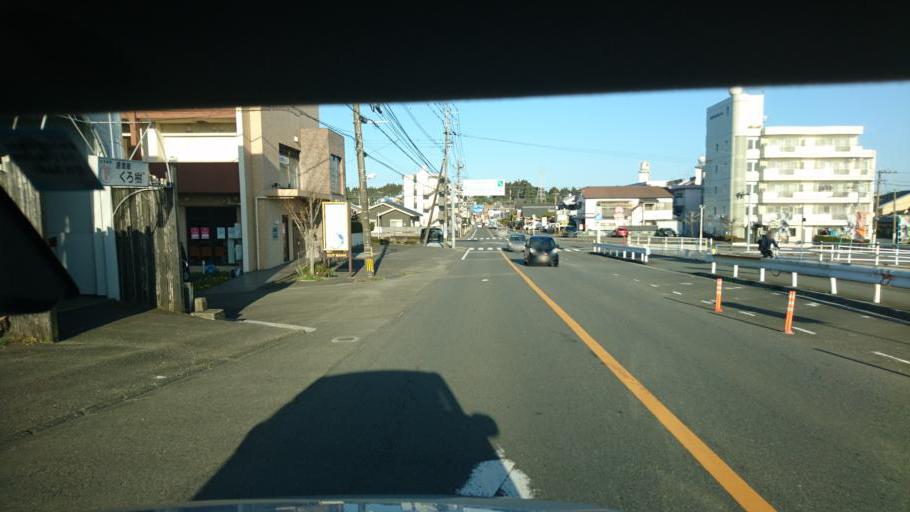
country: JP
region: Miyazaki
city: Miyazaki-shi
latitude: 31.8477
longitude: 131.3902
